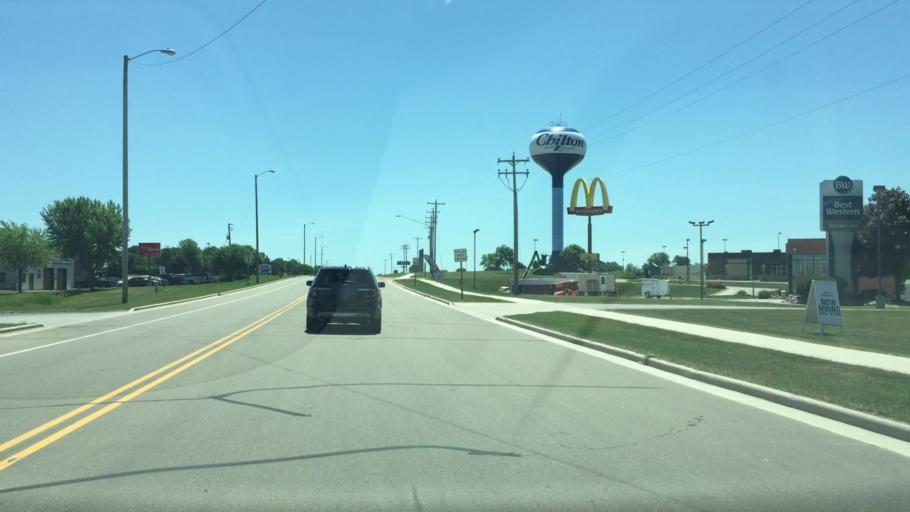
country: US
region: Wisconsin
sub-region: Calumet County
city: Chilton
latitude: 44.0208
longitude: -88.1535
